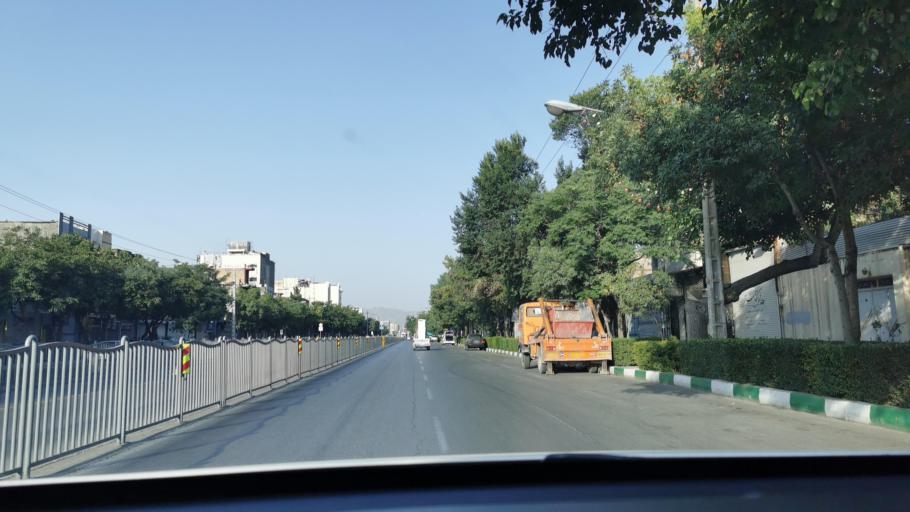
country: IR
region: Razavi Khorasan
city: Mashhad
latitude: 36.3049
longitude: 59.6426
